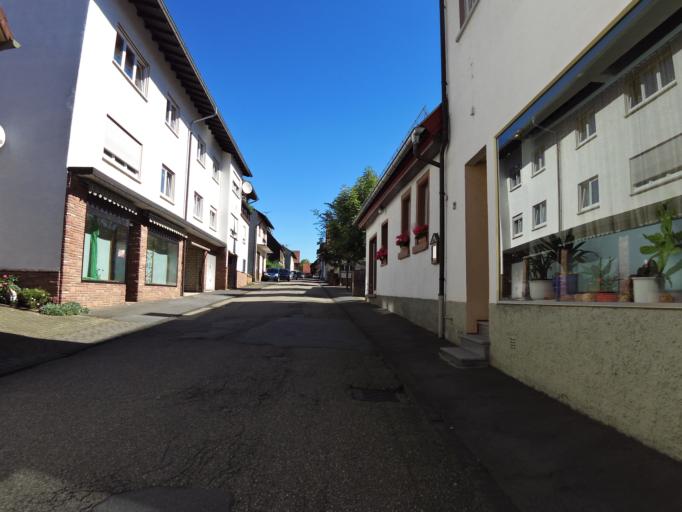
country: DE
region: Hesse
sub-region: Regierungsbezirk Darmstadt
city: Wald-Michelbach
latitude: 49.6278
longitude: 8.8577
